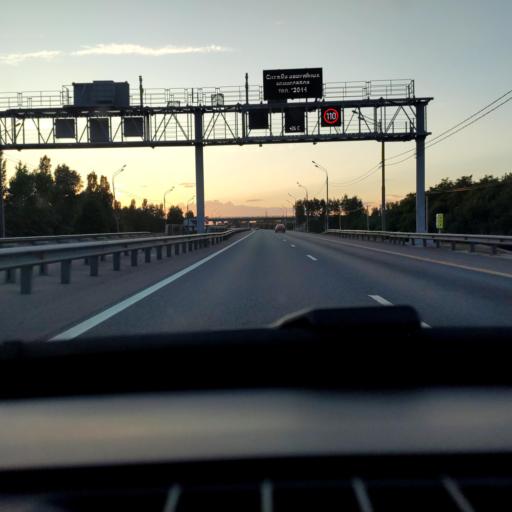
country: RU
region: Lipetsk
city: Khlevnoye
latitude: 52.2090
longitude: 39.1550
